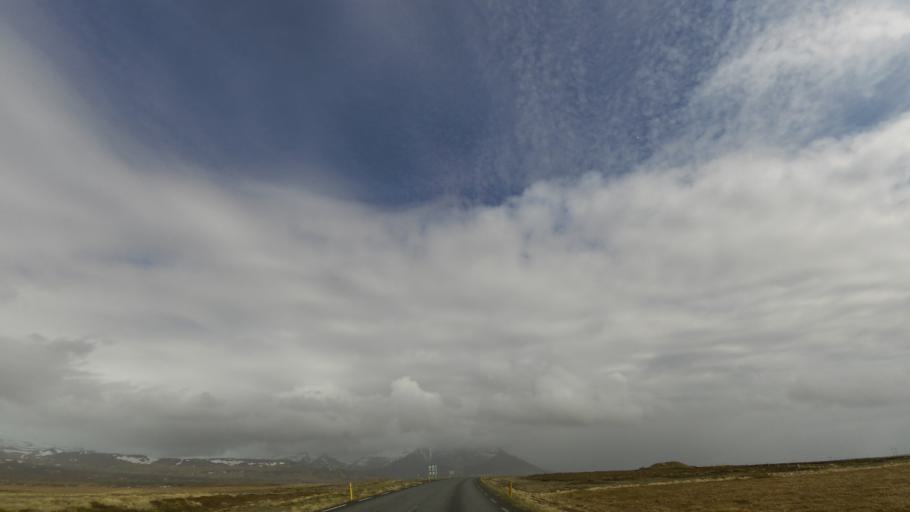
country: IS
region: West
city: Stykkisholmur
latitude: 64.8504
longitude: -22.7136
